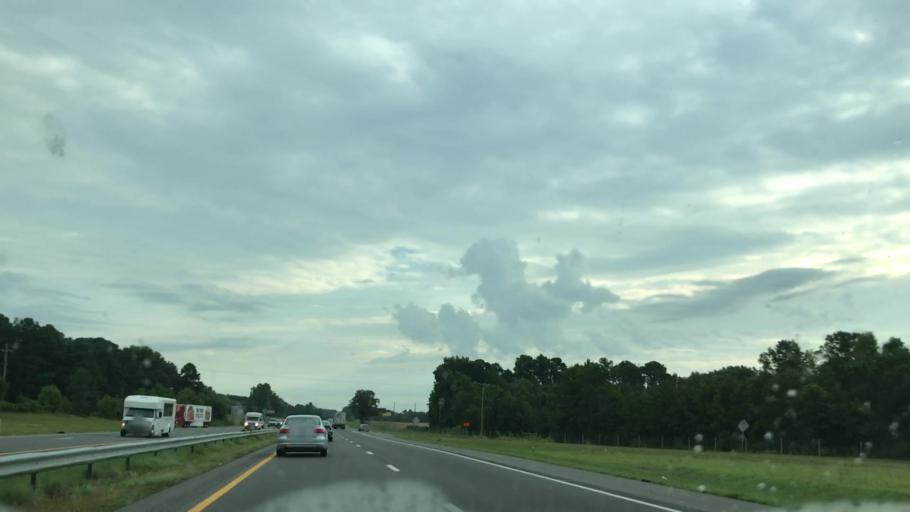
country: US
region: North Carolina
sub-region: Johnston County
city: Benson
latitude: 35.3439
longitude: -78.5575
